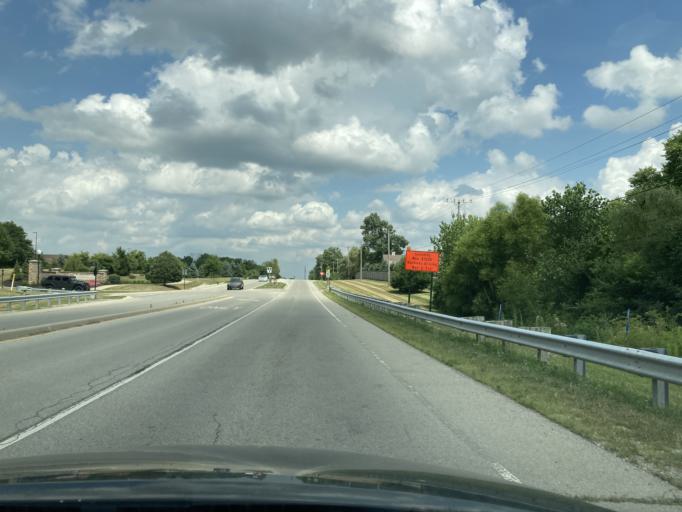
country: US
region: Indiana
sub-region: Boone County
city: Zionsville
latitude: 39.9986
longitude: -86.2504
